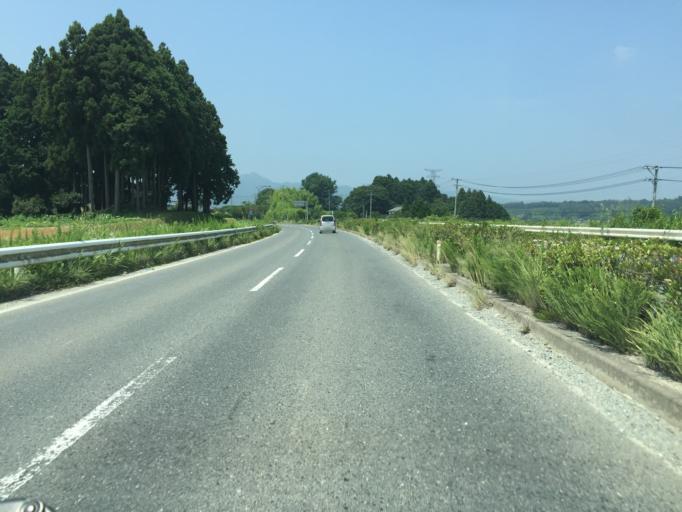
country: JP
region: Miyagi
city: Marumori
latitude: 37.8401
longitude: 140.9116
